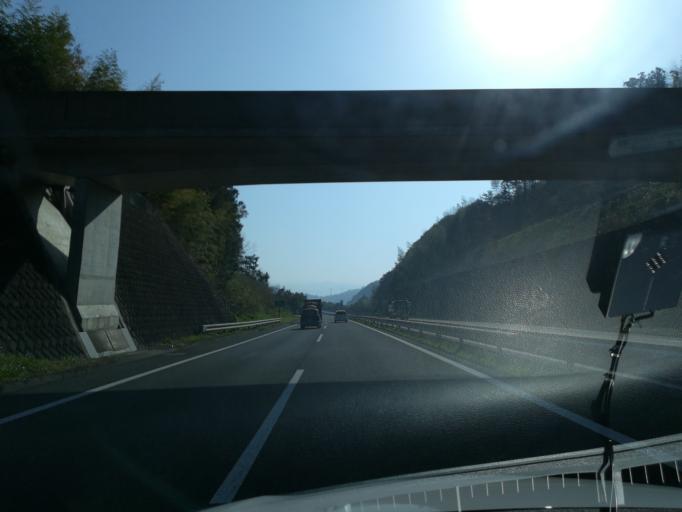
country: JP
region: Kochi
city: Kochi-shi
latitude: 33.5961
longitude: 133.5963
